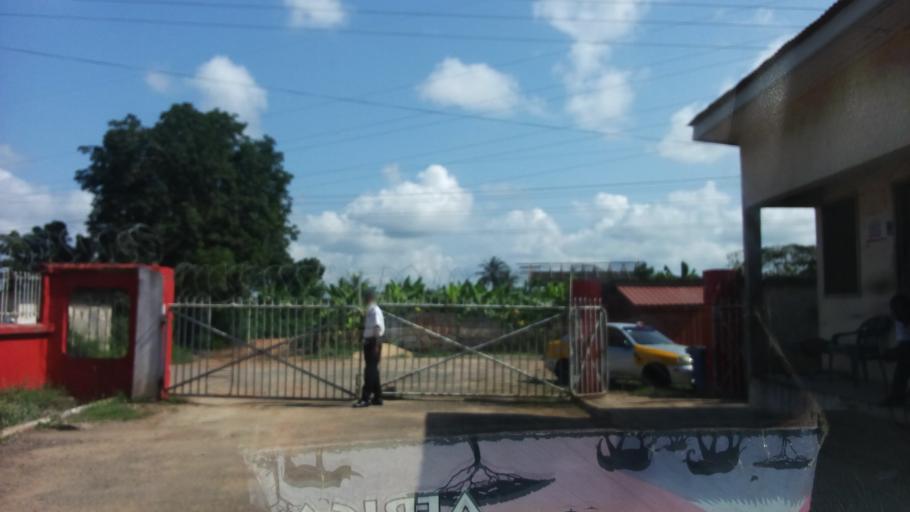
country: GH
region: Central
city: Cape Coast
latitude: 5.1223
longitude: -1.2737
